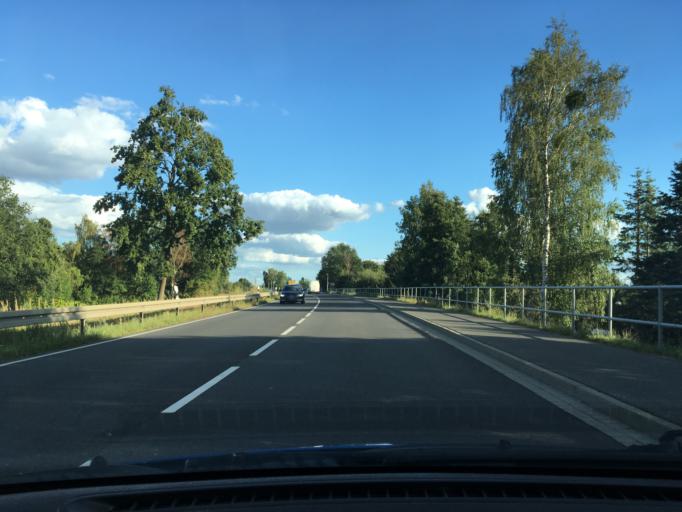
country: DE
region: Mecklenburg-Vorpommern
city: Grabow
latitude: 53.2779
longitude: 11.5557
